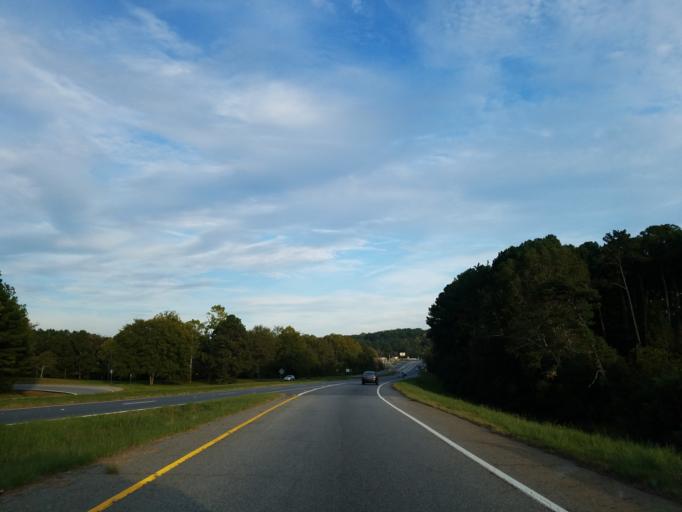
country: US
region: Georgia
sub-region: Bartow County
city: Cartersville
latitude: 34.2202
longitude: -84.8485
